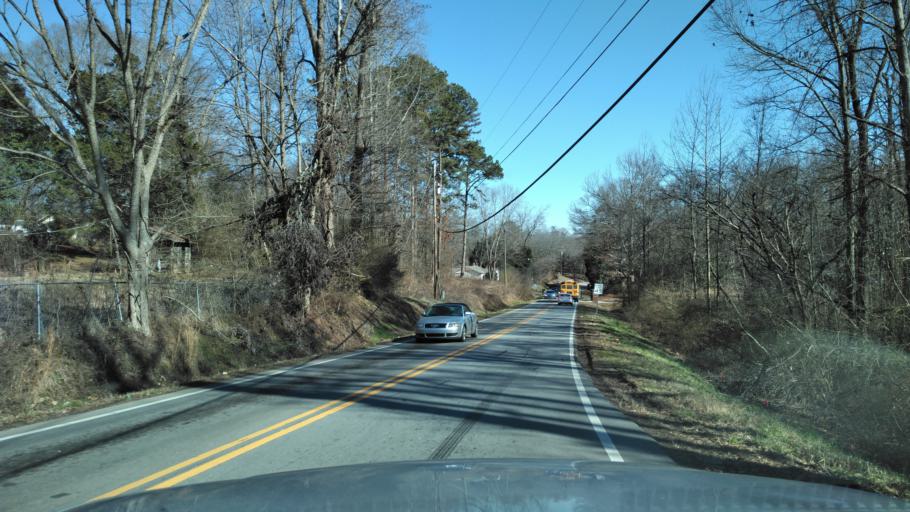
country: US
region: Georgia
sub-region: Hall County
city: Gainesville
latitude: 34.3177
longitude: -83.7591
